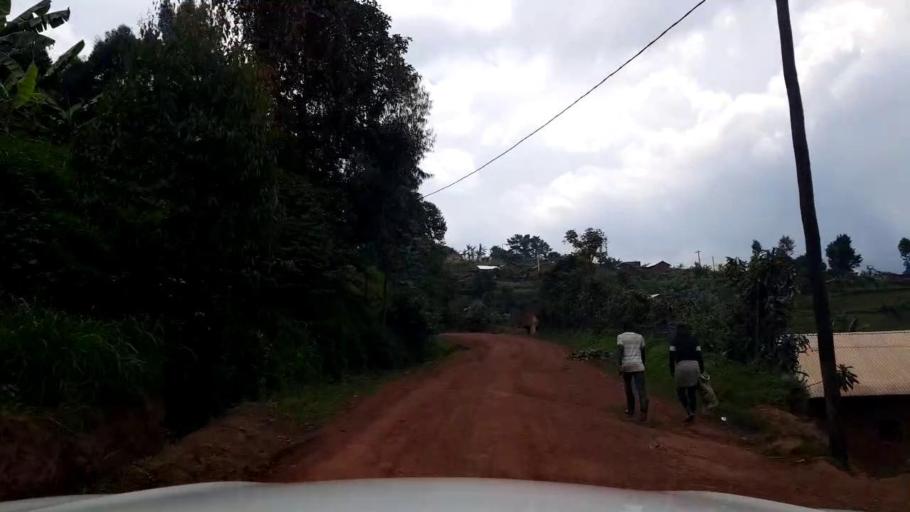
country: RW
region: Northern Province
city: Byumba
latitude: -1.4861
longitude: 29.9081
